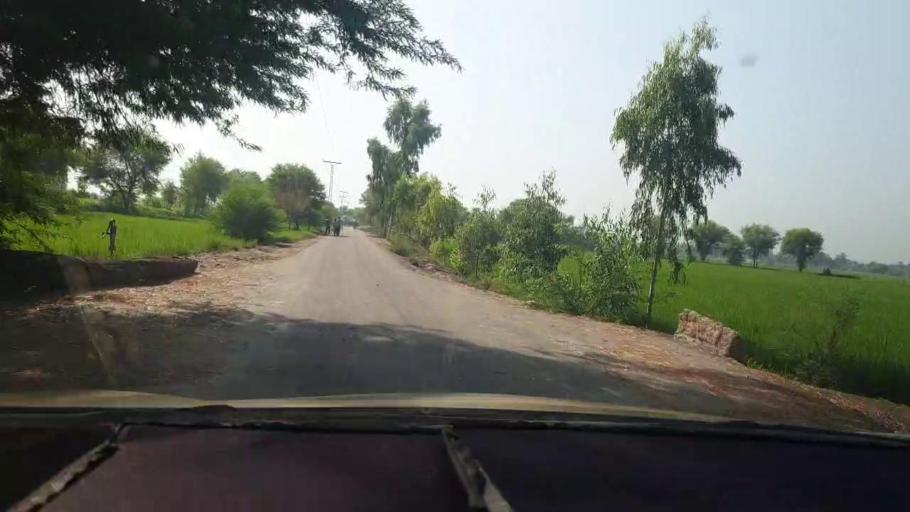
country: PK
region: Sindh
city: Kambar
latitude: 27.5792
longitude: 68.0737
